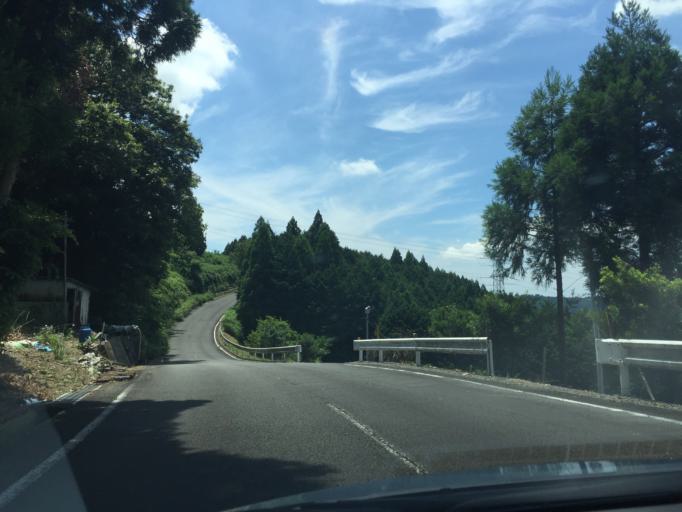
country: JP
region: Shizuoka
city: Kanaya
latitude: 34.8112
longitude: 138.0887
